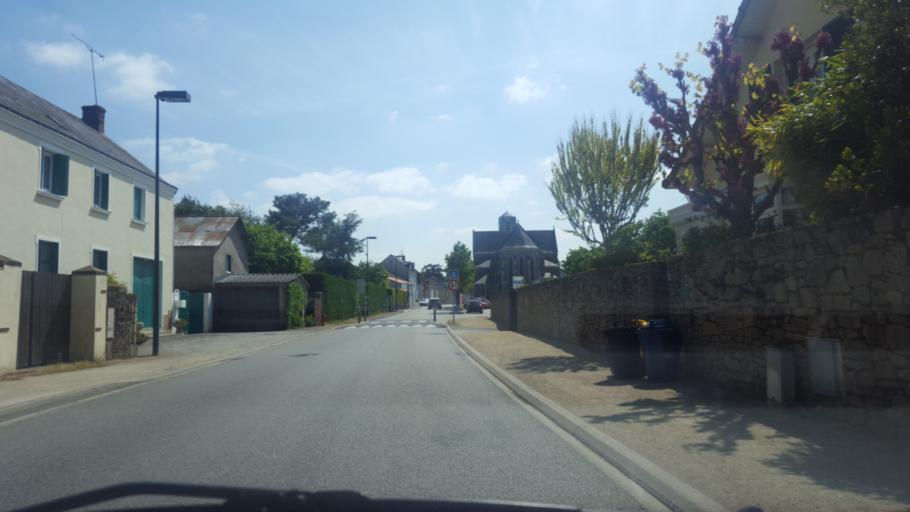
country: FR
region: Pays de la Loire
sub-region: Departement de la Loire-Atlantique
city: La Limouziniere
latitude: 46.9677
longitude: -1.5761
